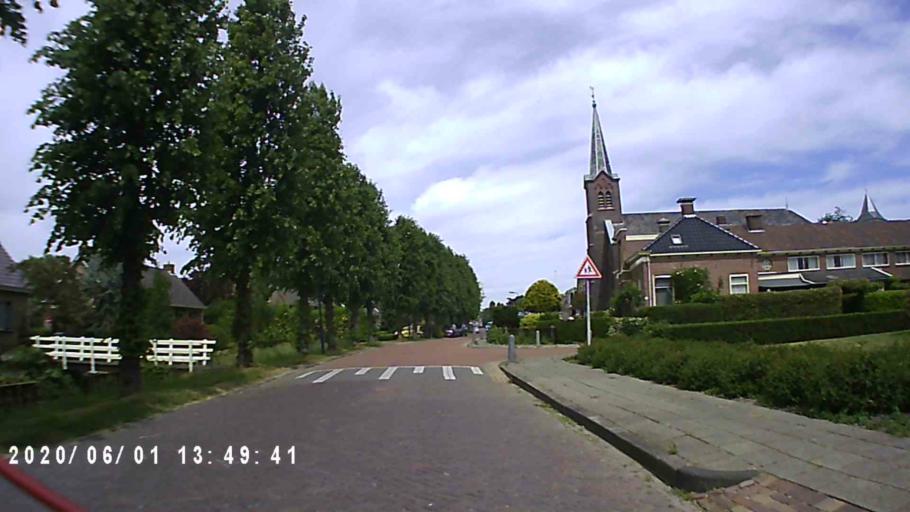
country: NL
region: Friesland
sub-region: Gemeente Littenseradiel
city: Wommels
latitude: 53.0961
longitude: 5.6171
